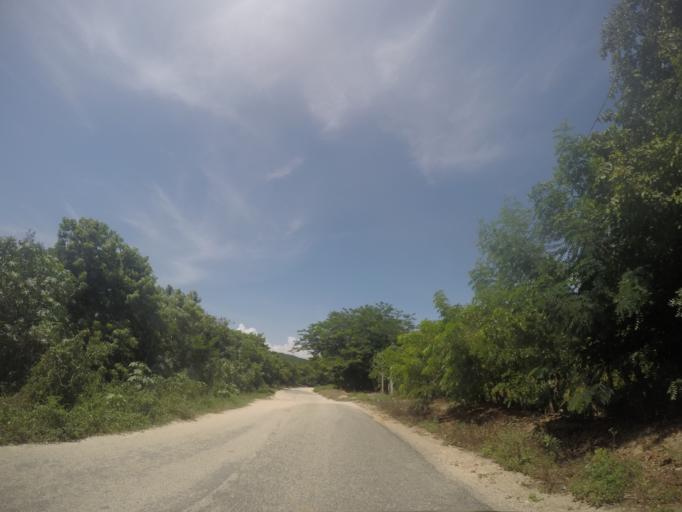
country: MX
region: Oaxaca
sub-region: Villa de Tututepec de Melchor Ocampo
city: Santa Rosa de Lima
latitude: 15.9913
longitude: -97.5399
